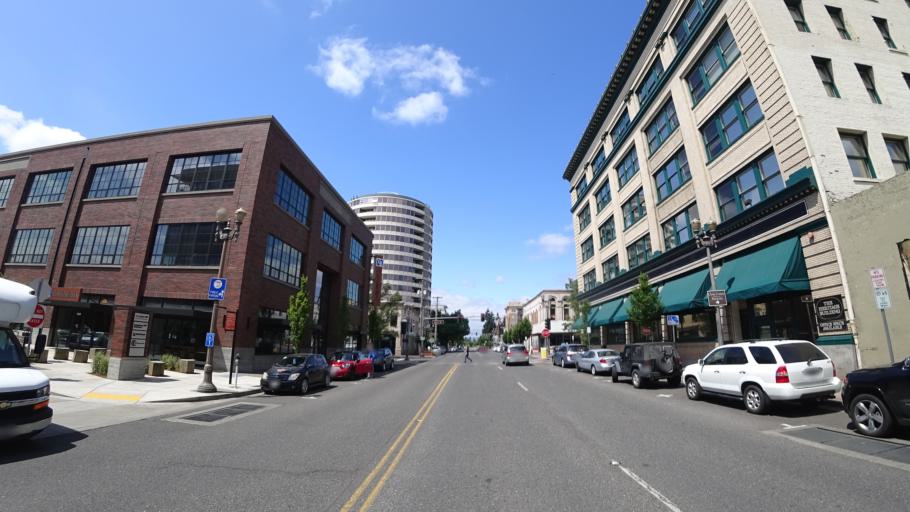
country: US
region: Washington
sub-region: Clark County
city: Vancouver
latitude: 45.6257
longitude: -122.6710
